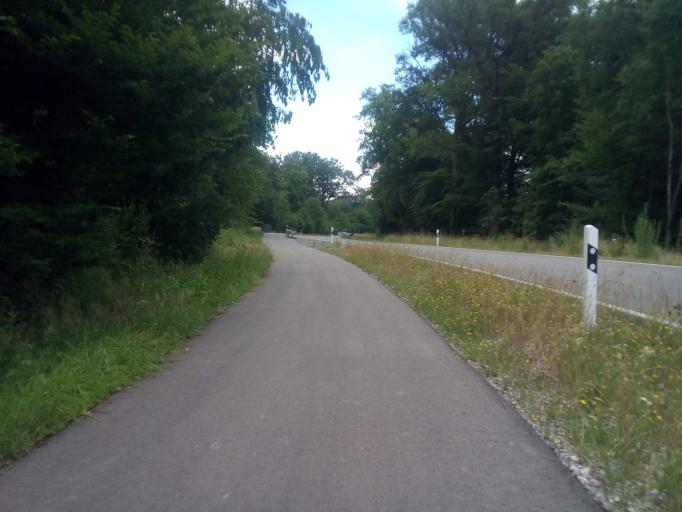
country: DE
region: Baden-Wuerttemberg
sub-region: Freiburg Region
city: Rheinau
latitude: 48.6370
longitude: 7.9474
